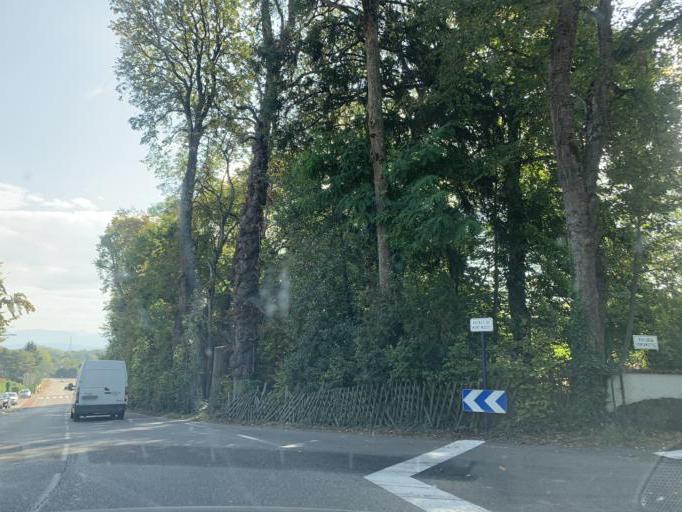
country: FR
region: Rhone-Alpes
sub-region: Departement de l'Ain
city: Divonne-les-Bains
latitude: 46.3497
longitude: 6.1324
